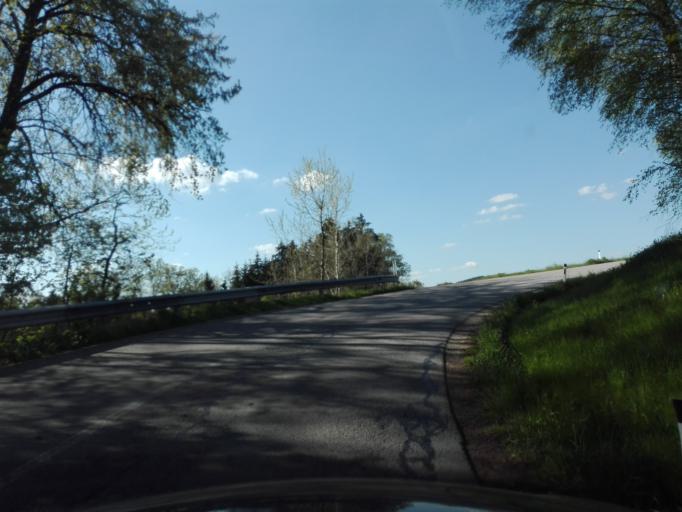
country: DE
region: Bavaria
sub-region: Lower Bavaria
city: Obernzell
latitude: 48.4981
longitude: 13.5781
